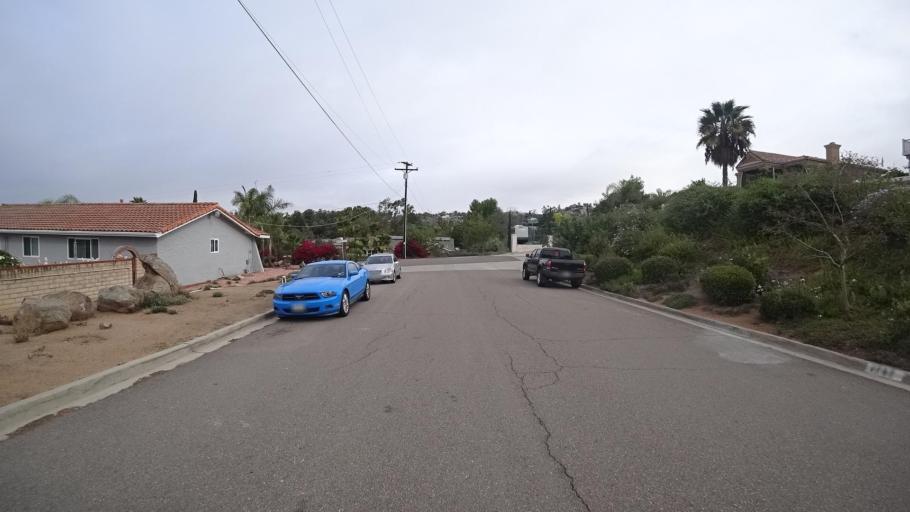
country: US
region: California
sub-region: San Diego County
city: Rancho San Diego
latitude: 32.7597
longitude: -116.9158
